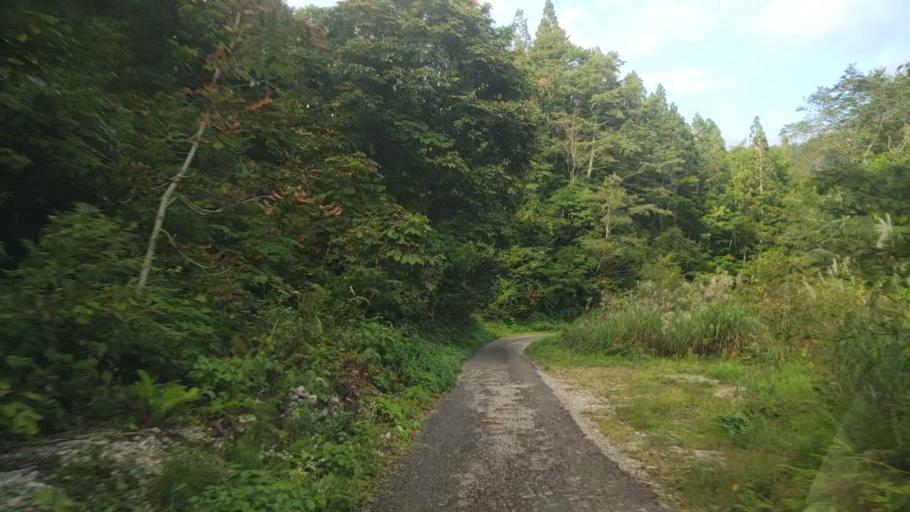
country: JP
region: Toyama
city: Yatsuomachi-higashikumisaka
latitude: 36.3645
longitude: 137.0723
